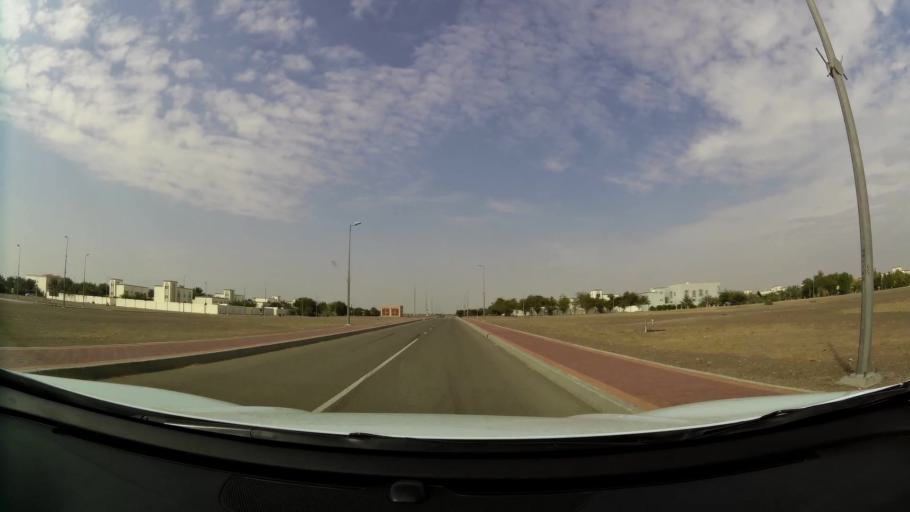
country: AE
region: Abu Dhabi
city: Al Ain
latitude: 24.0980
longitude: 55.8960
